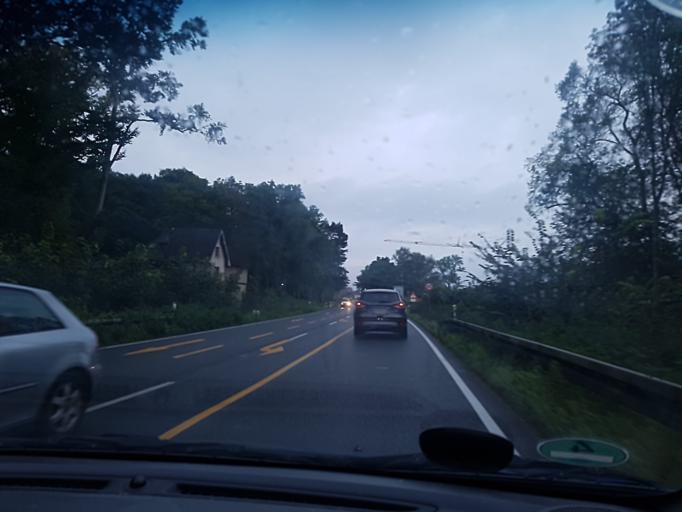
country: DE
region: Lower Saxony
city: Hemmingen
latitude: 52.3331
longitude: 9.7190
